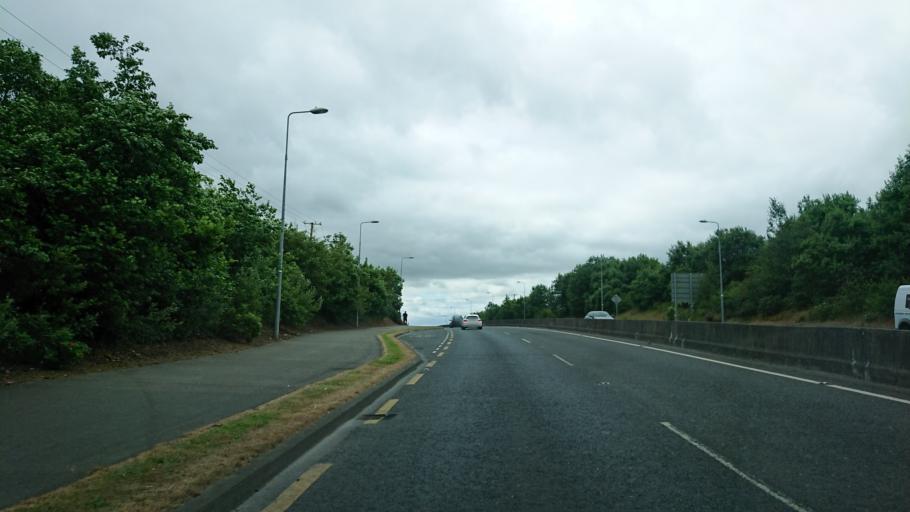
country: IE
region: Munster
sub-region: Waterford
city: Waterford
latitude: 52.2405
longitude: -7.0906
